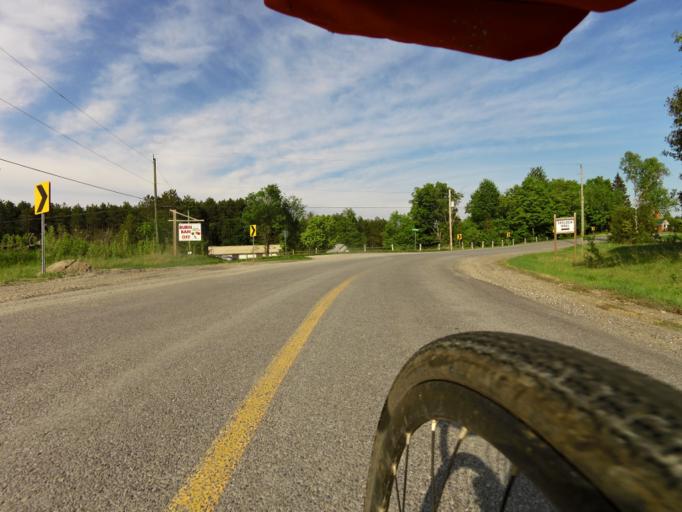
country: CA
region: Ontario
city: Arnprior
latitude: 45.1735
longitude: -76.4702
